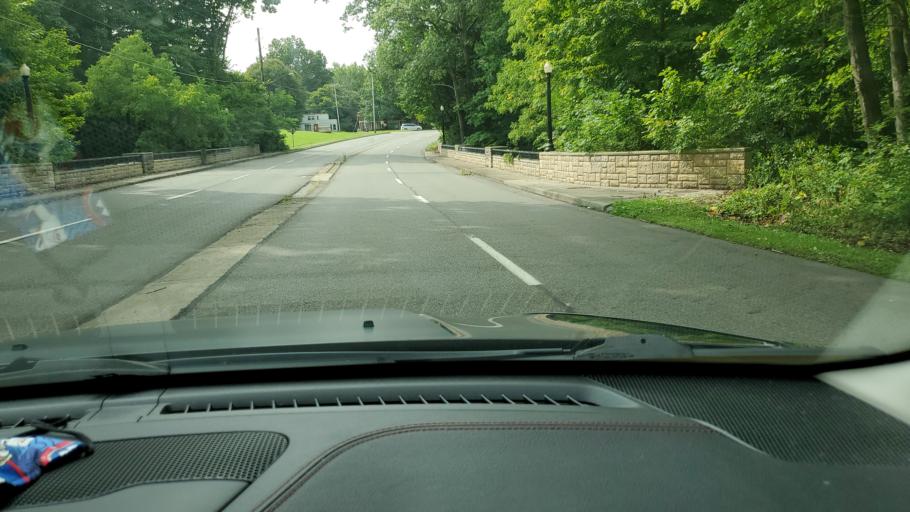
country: US
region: Ohio
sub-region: Mahoning County
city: Boardman
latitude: 41.0531
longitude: -80.6723
